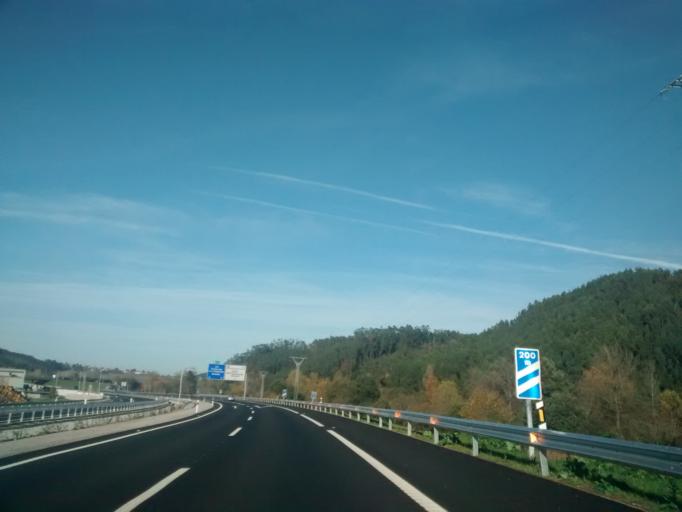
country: ES
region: Cantabria
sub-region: Provincia de Cantabria
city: Puente Viesgo
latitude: 43.3294
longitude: -3.9639
